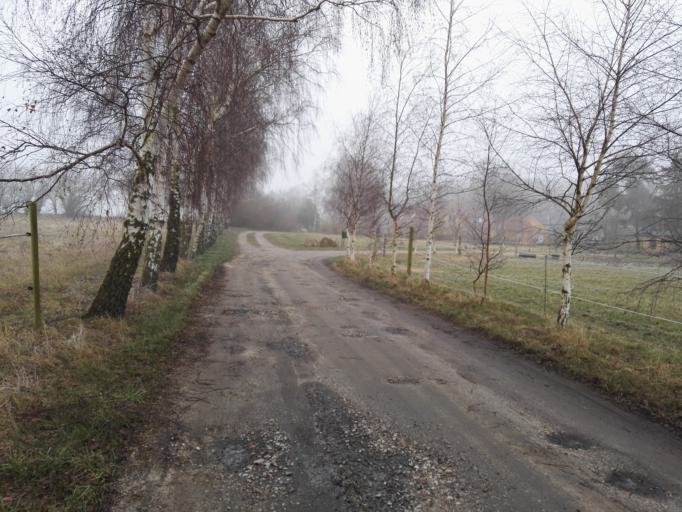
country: DK
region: Capital Region
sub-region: Frederikssund Kommune
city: Jaegerspris
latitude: 55.8446
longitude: 11.9940
